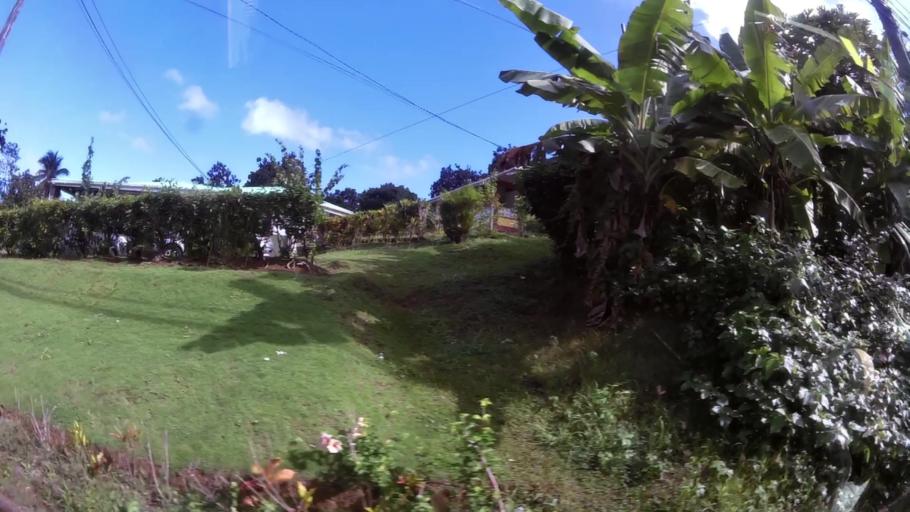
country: DM
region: Saint Andrew
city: Marigot
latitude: 15.5382
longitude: -61.2829
